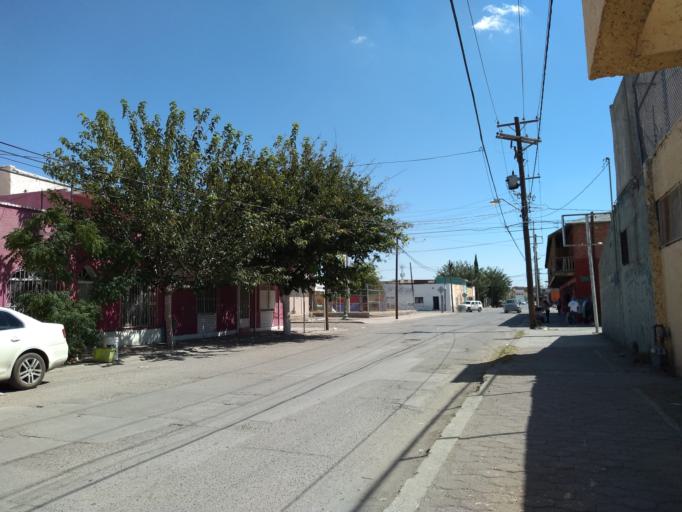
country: MX
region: Chihuahua
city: Ciudad Juarez
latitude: 31.7452
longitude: -106.4900
